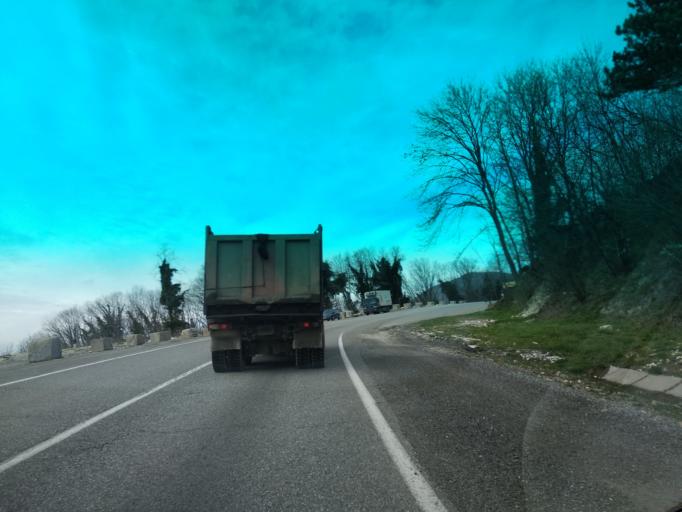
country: RU
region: Krasnodarskiy
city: Shepsi
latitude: 44.0714
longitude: 39.1355
